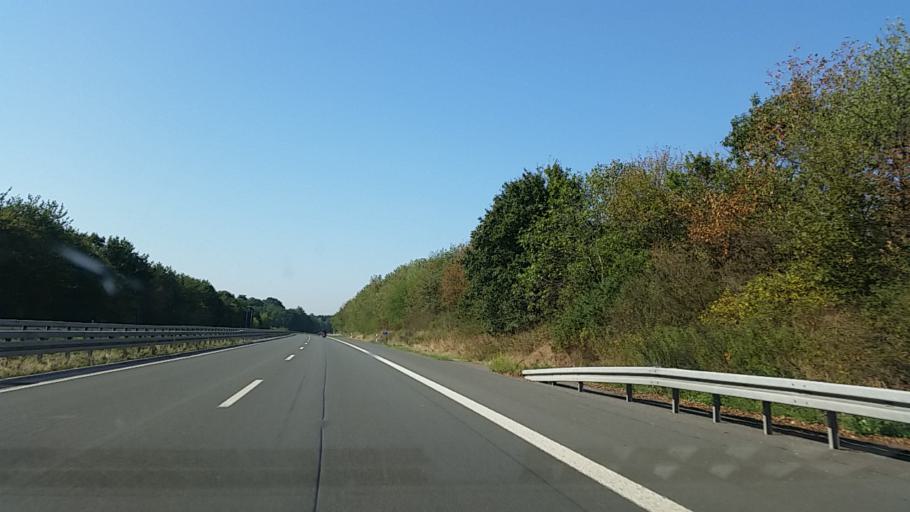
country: DE
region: North Rhine-Westphalia
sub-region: Regierungsbezirk Dusseldorf
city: Langenfeld
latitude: 51.1060
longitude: 6.9703
